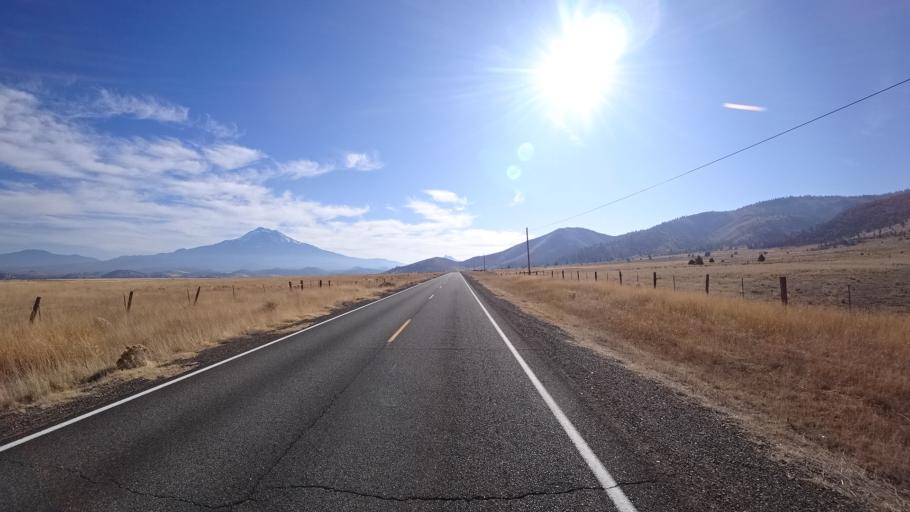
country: US
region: California
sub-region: Siskiyou County
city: Weed
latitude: 41.4833
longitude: -122.4968
